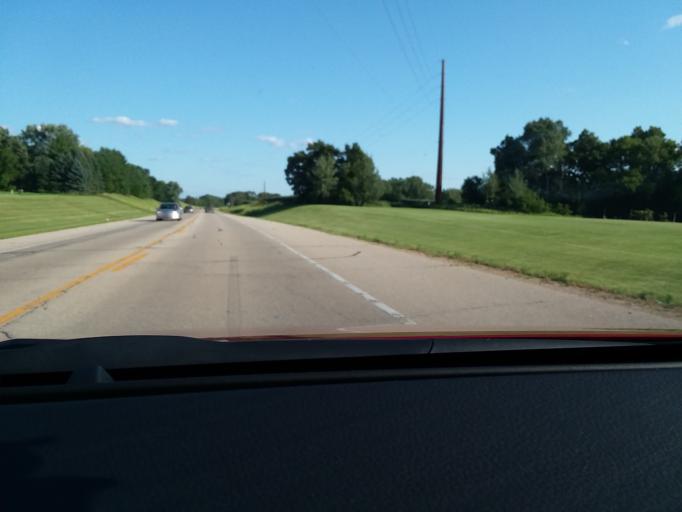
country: US
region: Wisconsin
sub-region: Dane County
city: Waunakee
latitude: 43.1714
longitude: -89.4109
